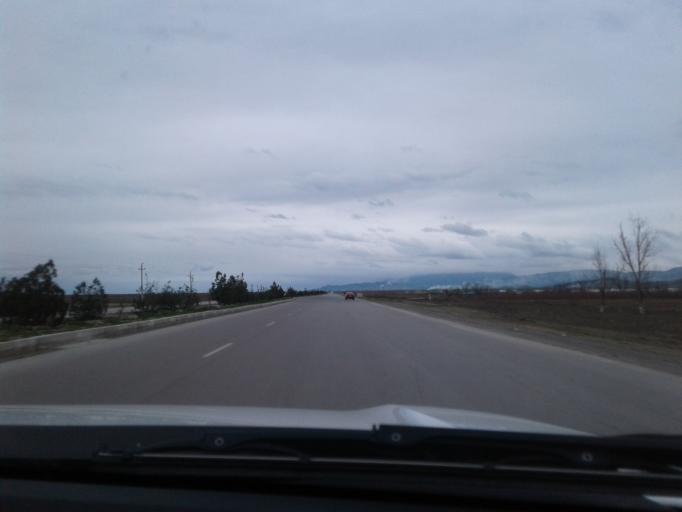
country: TM
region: Ahal
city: Baharly
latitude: 38.3868
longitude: 57.4919
